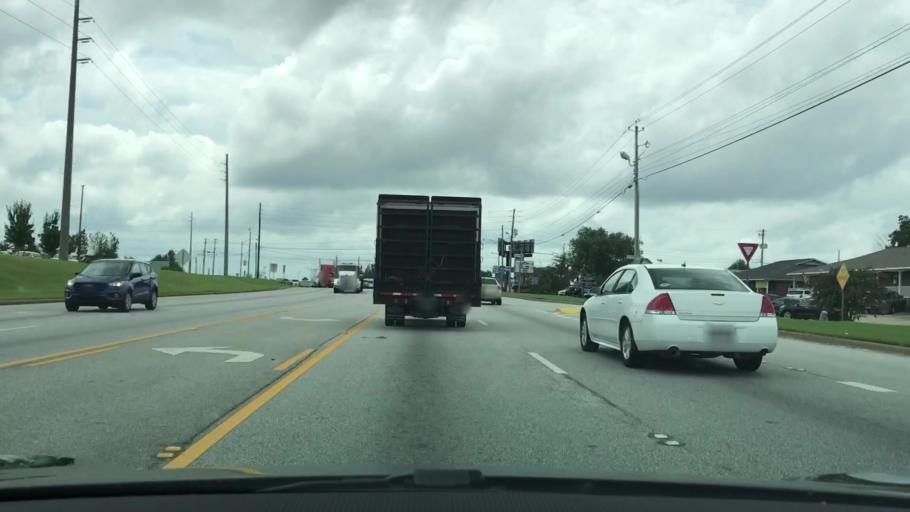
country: US
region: Alabama
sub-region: Lee County
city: Opelika
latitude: 32.6246
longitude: -85.4052
